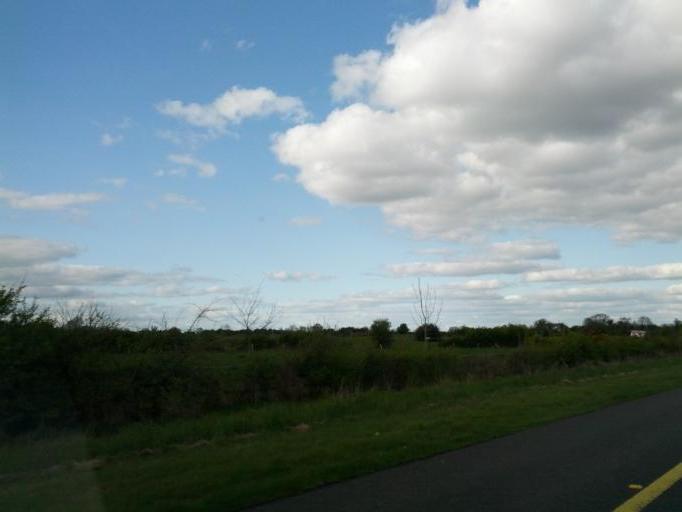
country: IE
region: Connaught
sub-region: County Galway
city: Ballinasloe
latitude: 53.3312
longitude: -8.1201
